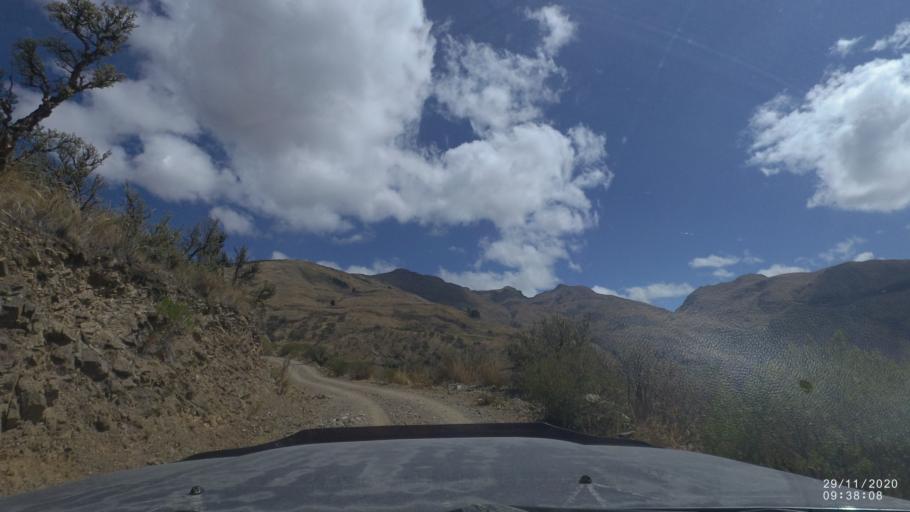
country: BO
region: Cochabamba
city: Cochabamba
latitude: -17.3086
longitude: -66.1846
